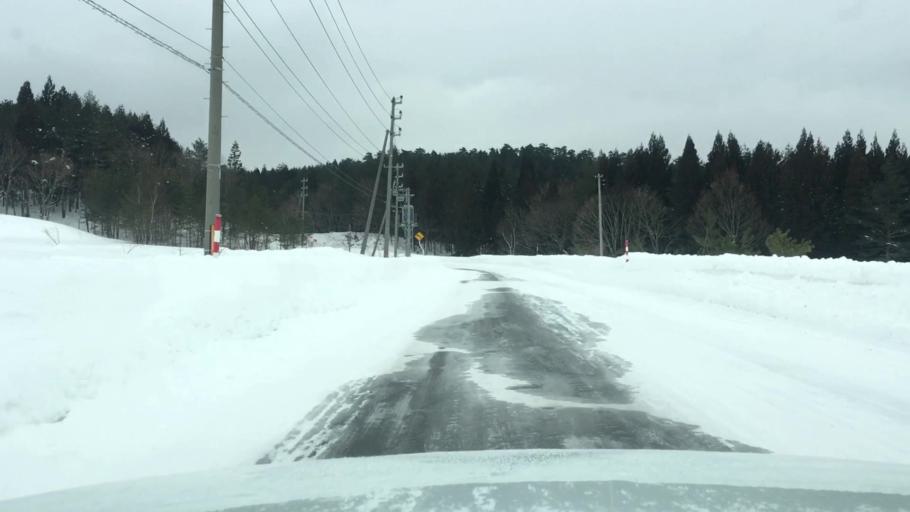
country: JP
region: Akita
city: Hanawa
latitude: 39.9934
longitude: 140.9955
